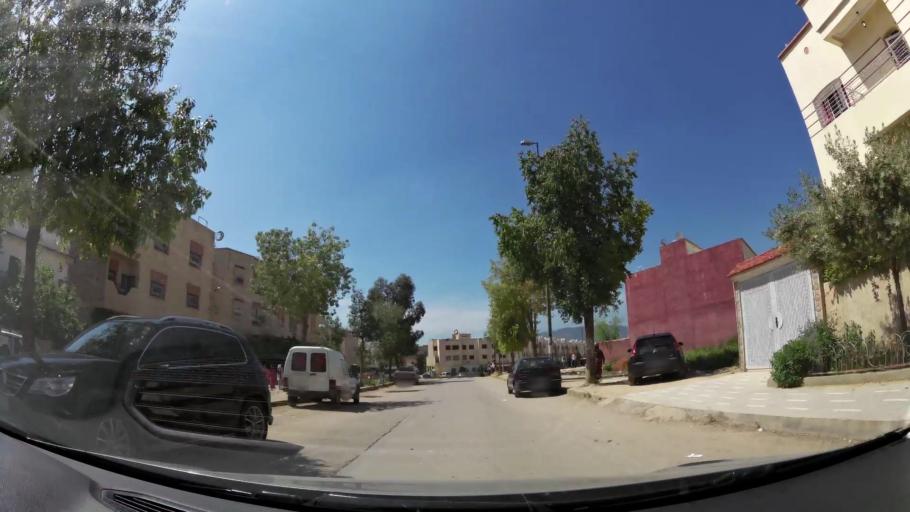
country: MA
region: Fes-Boulemane
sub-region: Fes
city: Fes
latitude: 34.0154
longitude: -5.0265
